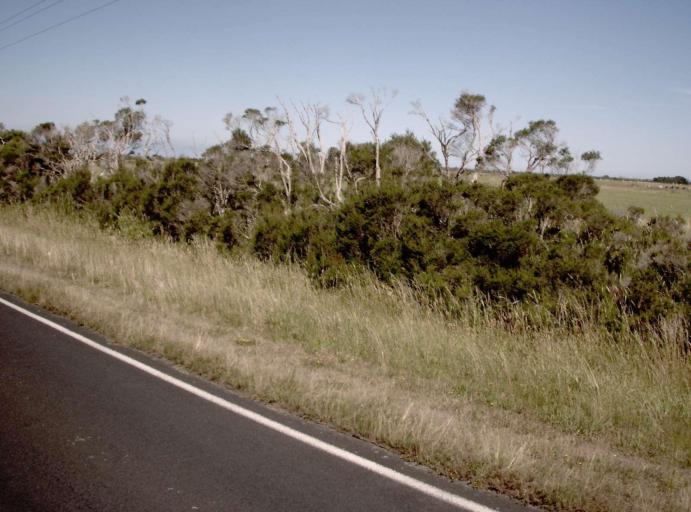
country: AU
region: Victoria
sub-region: Latrobe
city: Traralgon
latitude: -38.6289
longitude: 146.5981
